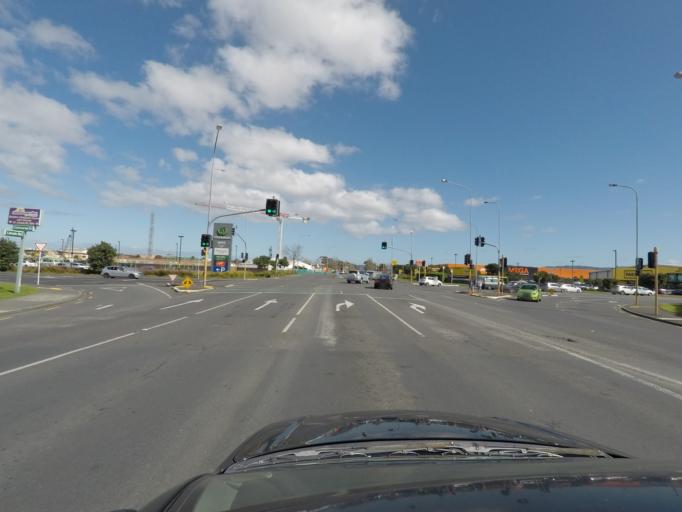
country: NZ
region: Auckland
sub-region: Auckland
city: Rosebank
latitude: -36.8565
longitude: 174.6300
